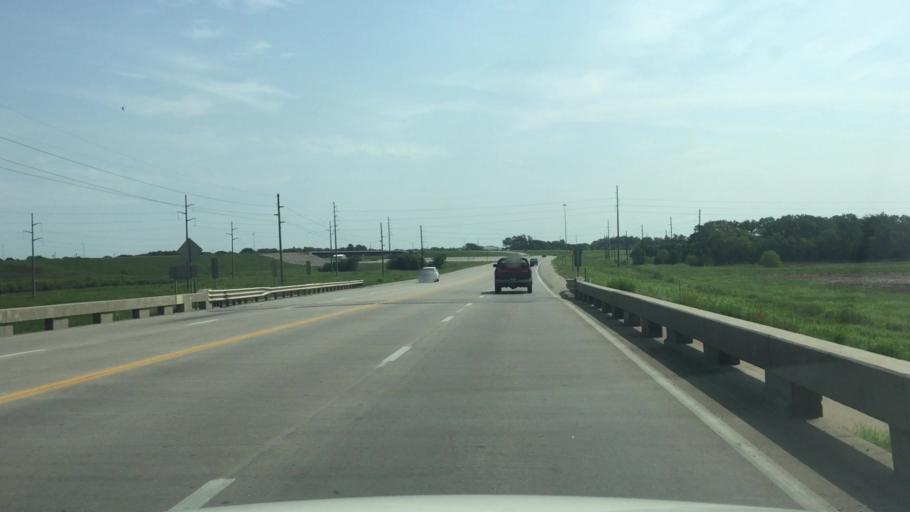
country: US
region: Kansas
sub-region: Montgomery County
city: Coffeyville
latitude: 37.0425
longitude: -95.5898
